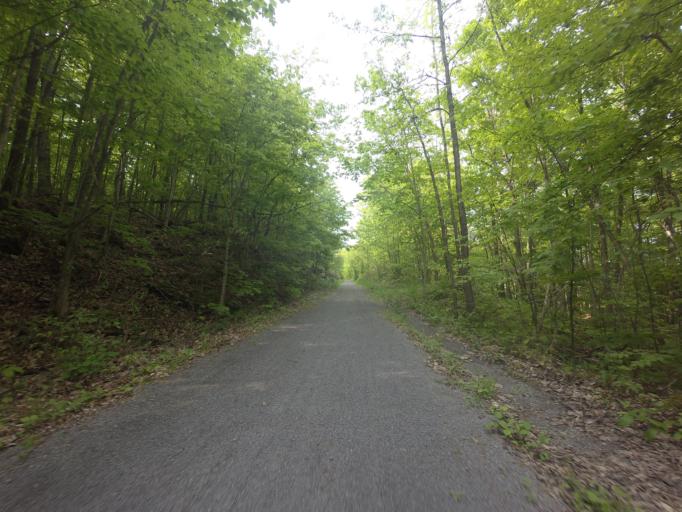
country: CA
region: Ontario
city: Kingston
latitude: 44.3949
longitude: -76.6407
